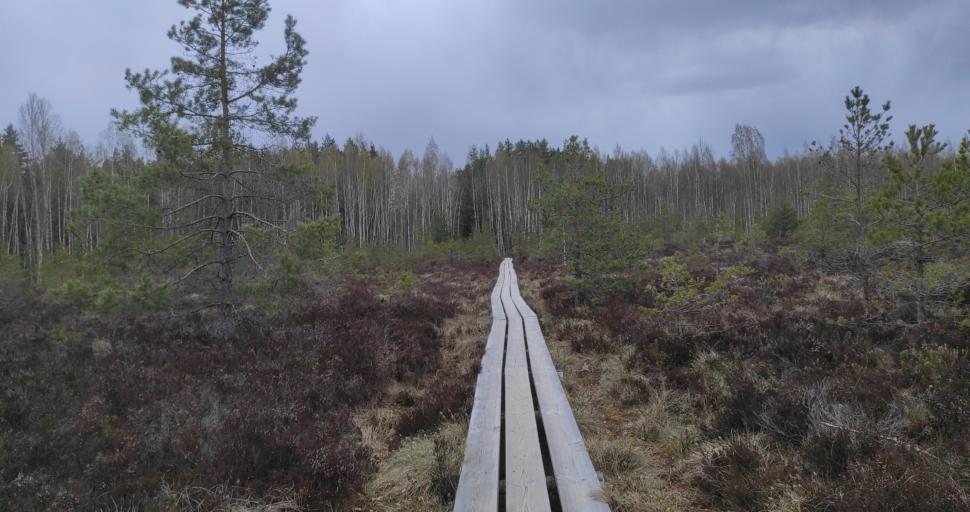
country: LV
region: Dundaga
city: Dundaga
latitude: 57.3554
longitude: 22.1540
